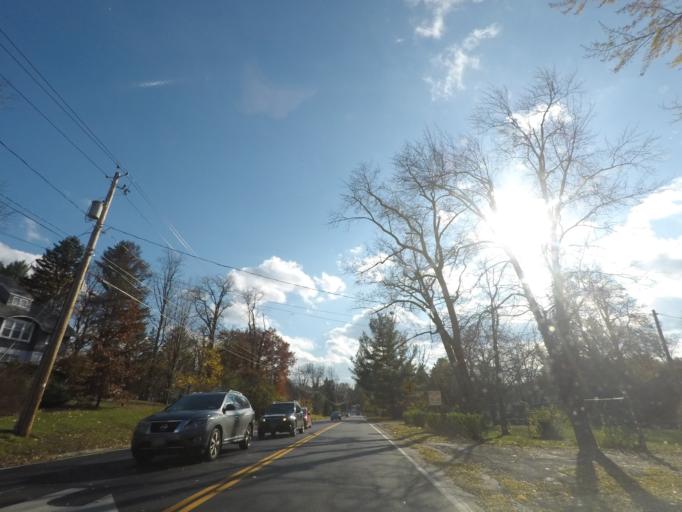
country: US
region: New York
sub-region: Schenectady County
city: Schenectady
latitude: 42.7958
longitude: -73.8934
